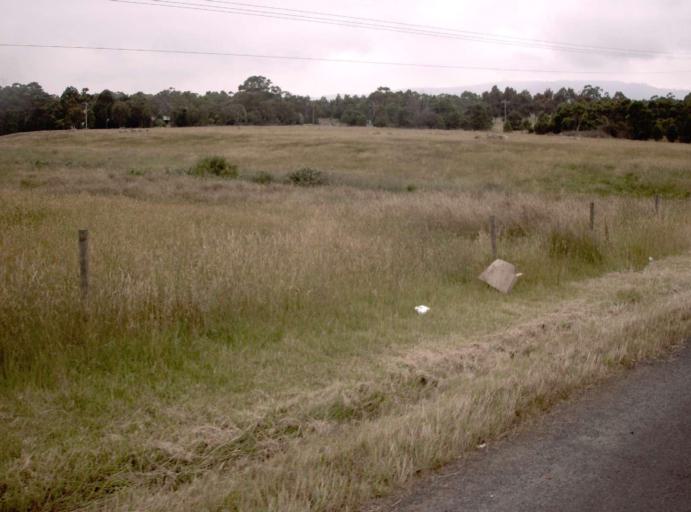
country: AU
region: Victoria
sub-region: Latrobe
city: Morwell
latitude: -38.2994
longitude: 146.4182
